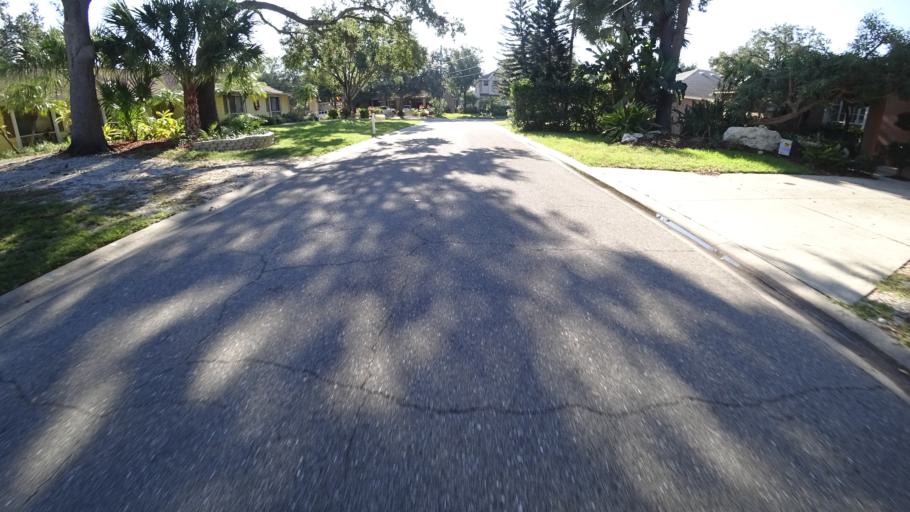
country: US
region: Florida
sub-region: Manatee County
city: Ellenton
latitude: 27.5010
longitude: -82.5053
